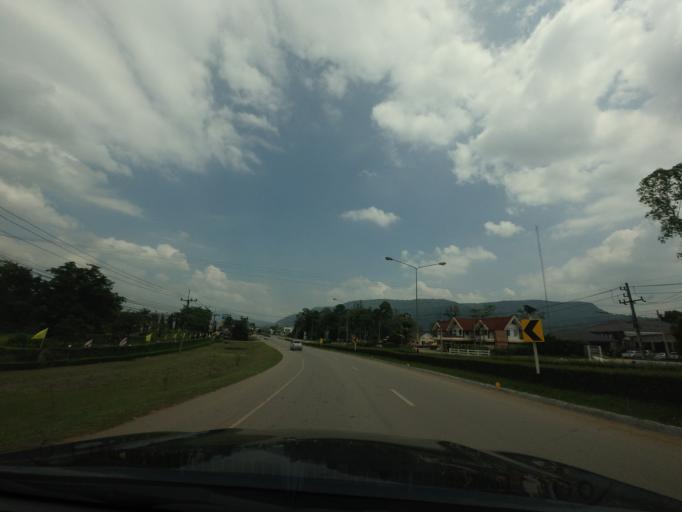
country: TH
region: Loei
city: Phu Ruea
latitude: 17.4492
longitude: 101.3545
